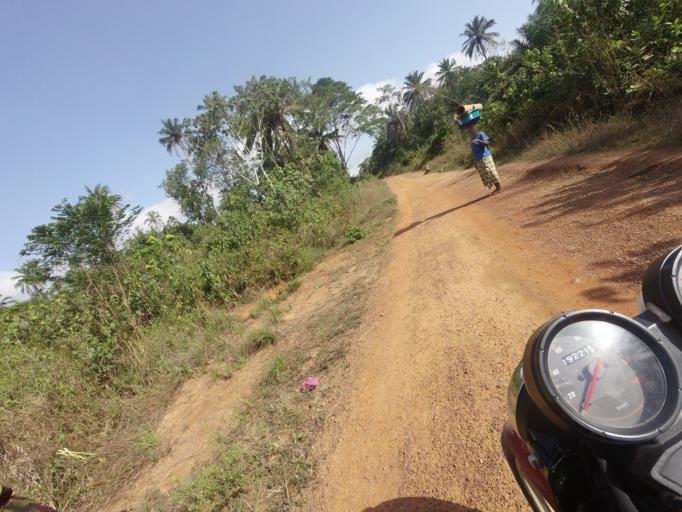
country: LR
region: Nimba
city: New Yekepa
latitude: 7.6179
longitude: -8.6288
